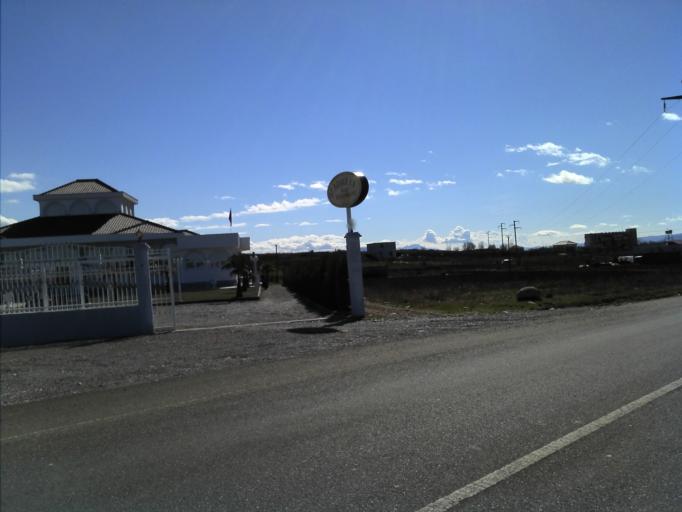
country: AL
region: Shkoder
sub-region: Rrethi i Malesia e Madhe
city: Koplik
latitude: 42.1941
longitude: 19.4559
